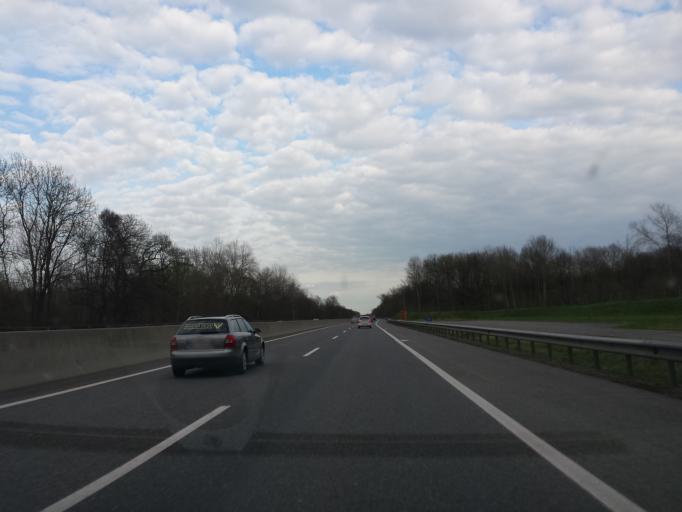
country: AT
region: Lower Austria
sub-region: Politischer Bezirk Korneuburg
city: Stetteldorf am Wagram
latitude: 48.3663
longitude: 15.9527
